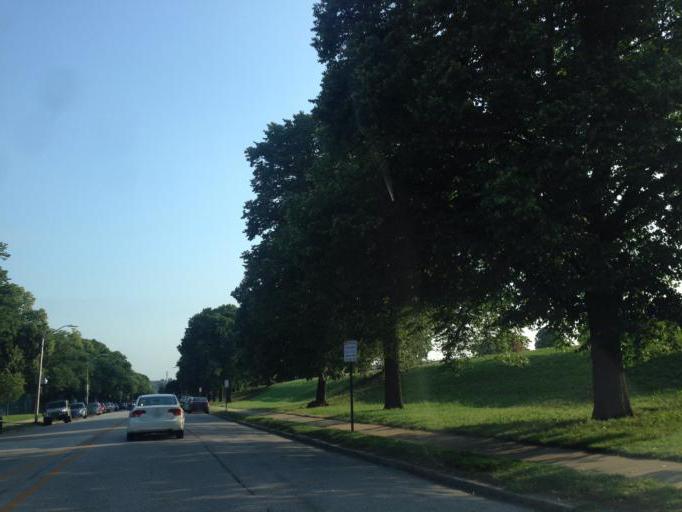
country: US
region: Maryland
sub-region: City of Baltimore
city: Baltimore
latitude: 39.2879
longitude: -76.5759
